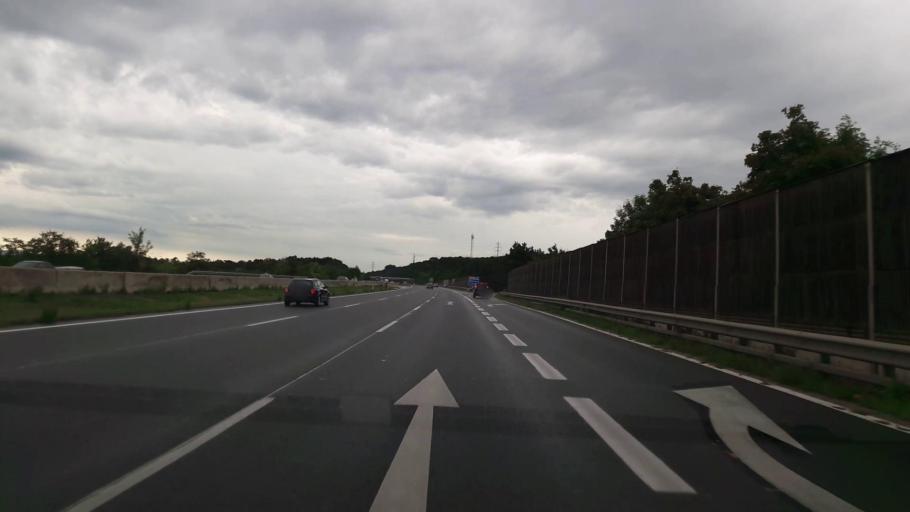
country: AT
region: Lower Austria
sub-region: Politischer Bezirk Wiener Neustadt
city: Theresienfeld
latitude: 47.8611
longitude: 16.1867
